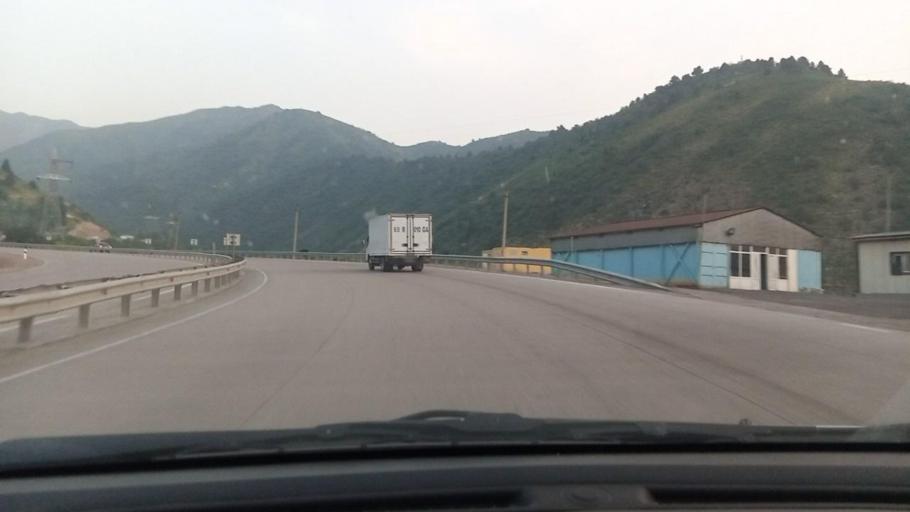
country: UZ
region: Toshkent
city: Angren
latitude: 41.1527
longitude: 70.4444
